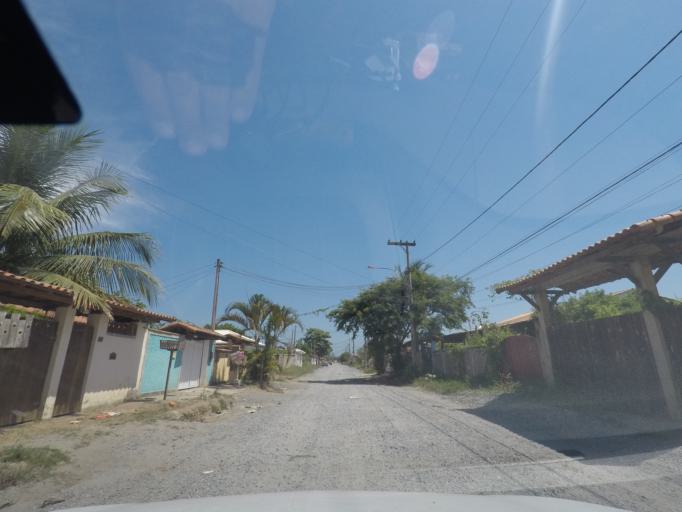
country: BR
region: Rio de Janeiro
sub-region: Marica
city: Marica
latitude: -22.9573
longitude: -42.9568
